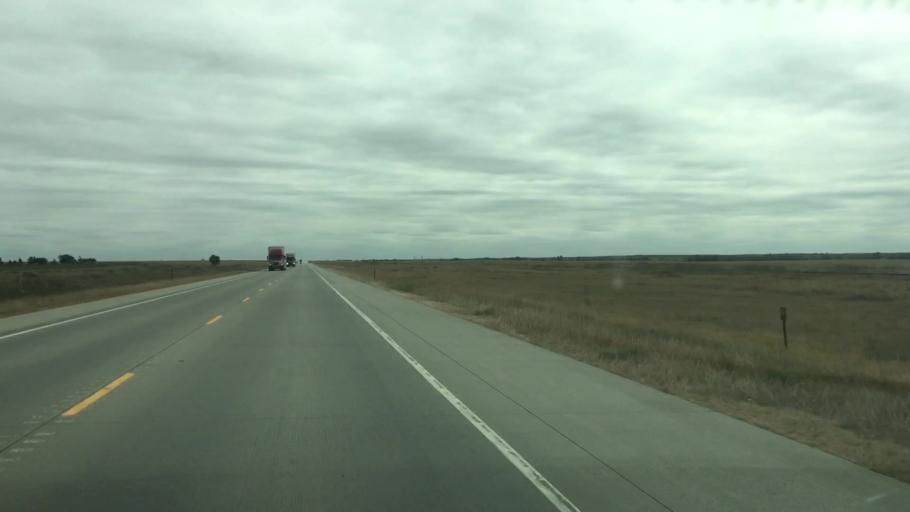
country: US
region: Colorado
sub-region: Kiowa County
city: Eads
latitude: 38.7792
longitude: -102.8959
